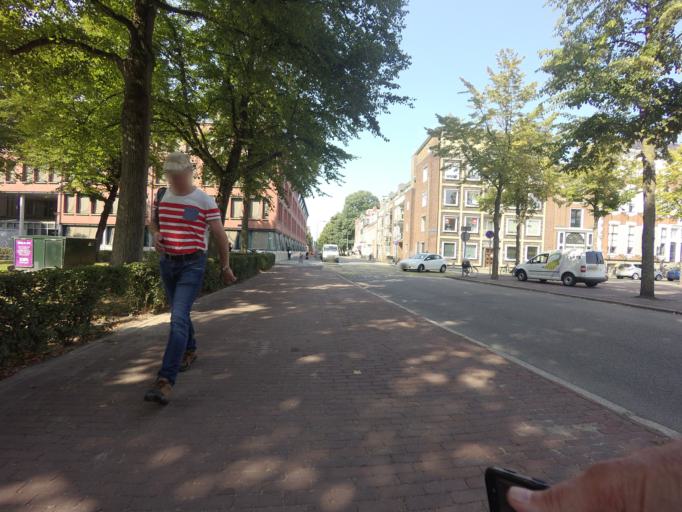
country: NL
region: Groningen
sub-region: Gemeente Groningen
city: Groningen
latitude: 53.2217
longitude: 6.5622
